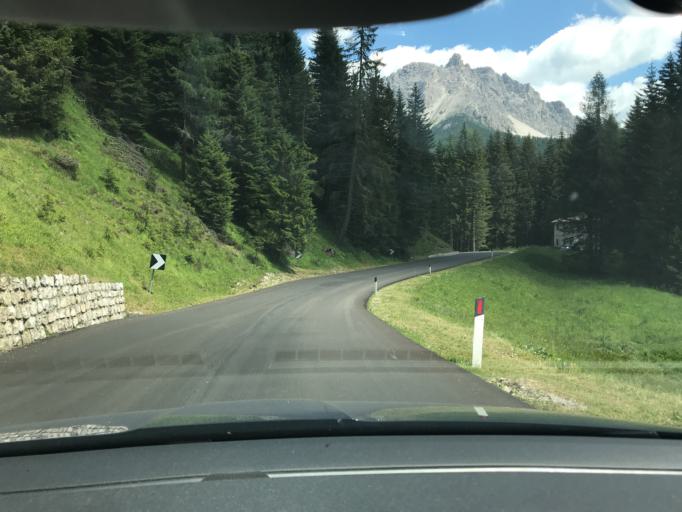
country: IT
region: Veneto
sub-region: Provincia di Belluno
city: Cortina d'Ampezzo
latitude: 46.5605
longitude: 12.2361
